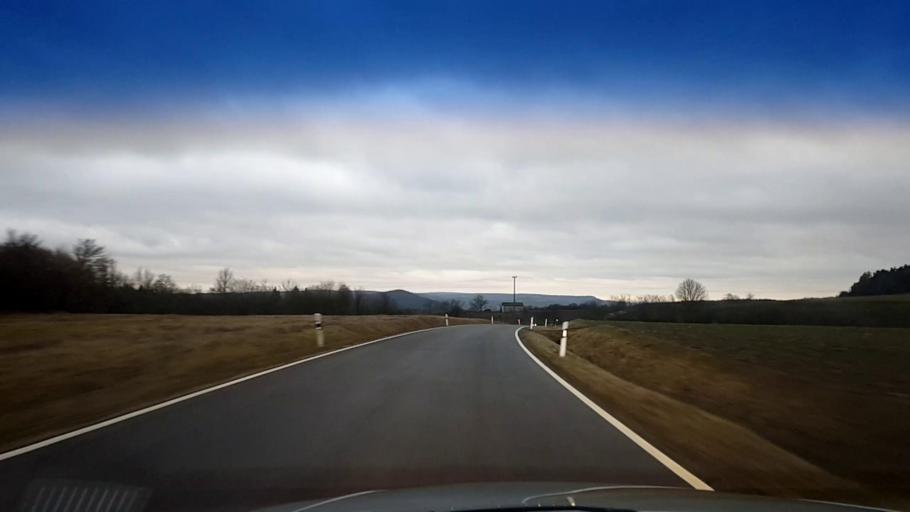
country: DE
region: Bavaria
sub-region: Upper Franconia
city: Wattendorf
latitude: 50.0308
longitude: 11.0658
